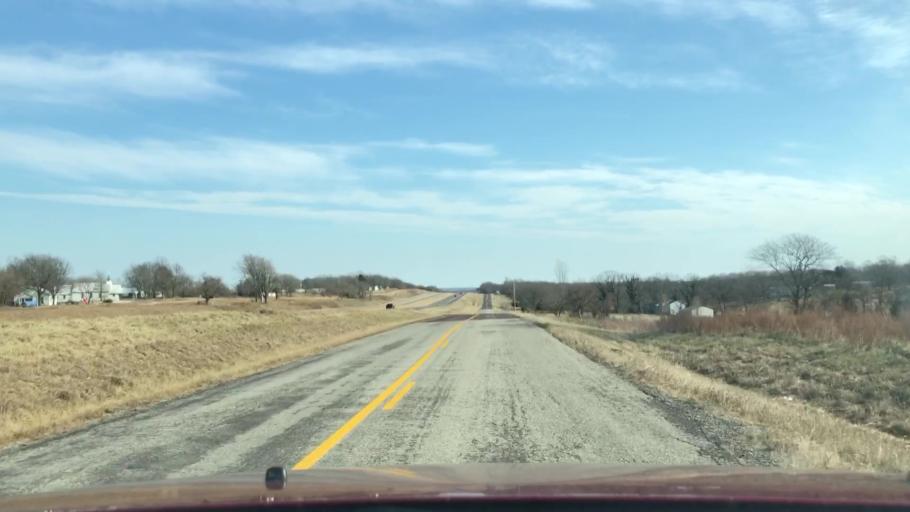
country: US
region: Missouri
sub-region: Wright County
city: Mansfield
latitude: 37.1113
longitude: -92.6365
